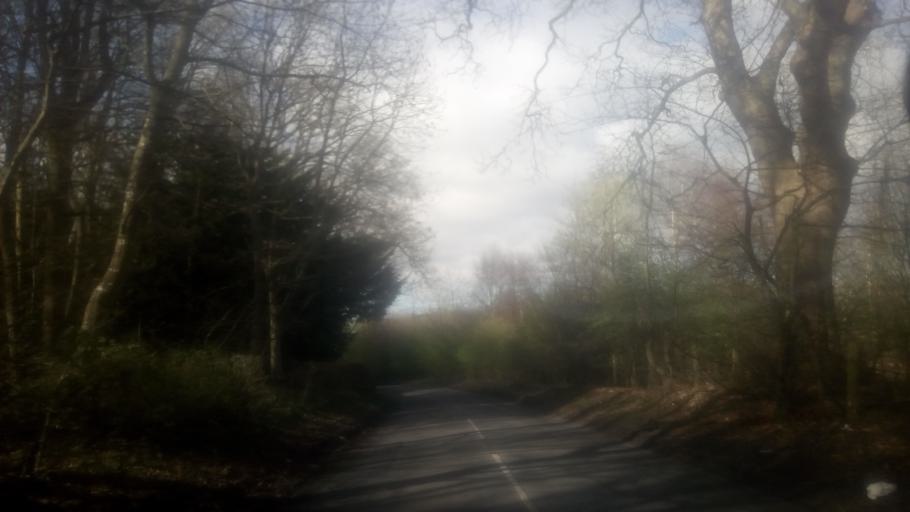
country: GB
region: Scotland
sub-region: East Lothian
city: Ormiston
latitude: 55.8938
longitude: -2.9553
